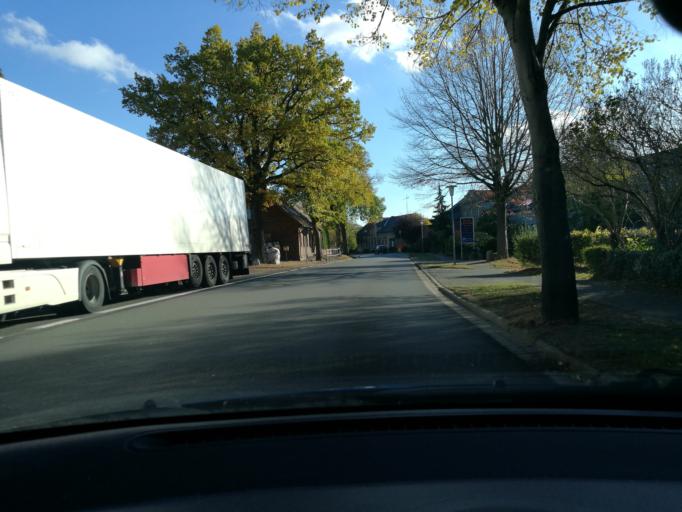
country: DE
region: Brandenburg
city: Karstadt
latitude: 53.1348
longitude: 11.7828
